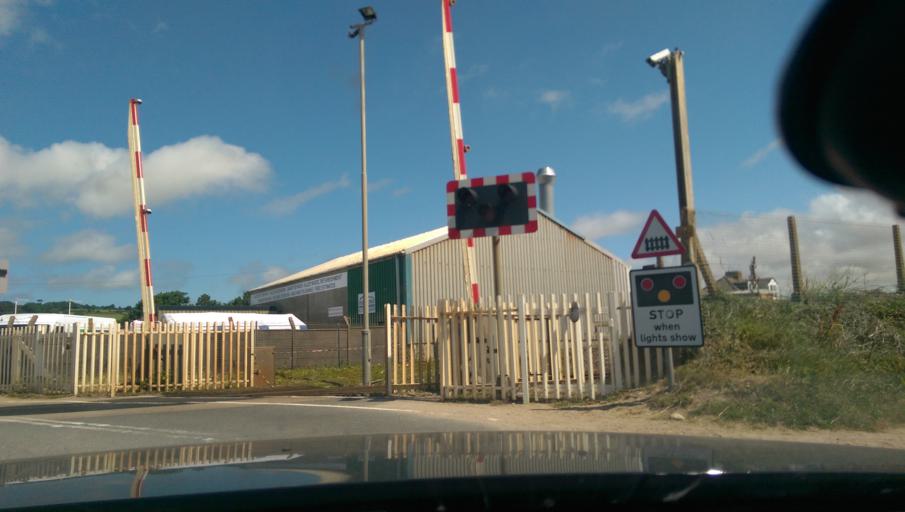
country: GB
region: England
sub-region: Cornwall
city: Marazion
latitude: 50.1282
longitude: -5.5023
